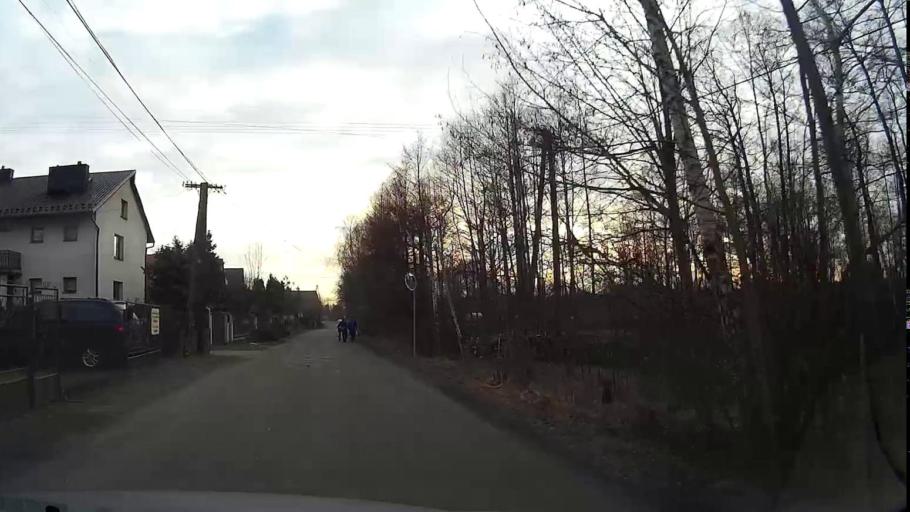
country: PL
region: Lesser Poland Voivodeship
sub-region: Powiat chrzanowski
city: Alwernia
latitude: 50.0599
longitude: 19.5288
